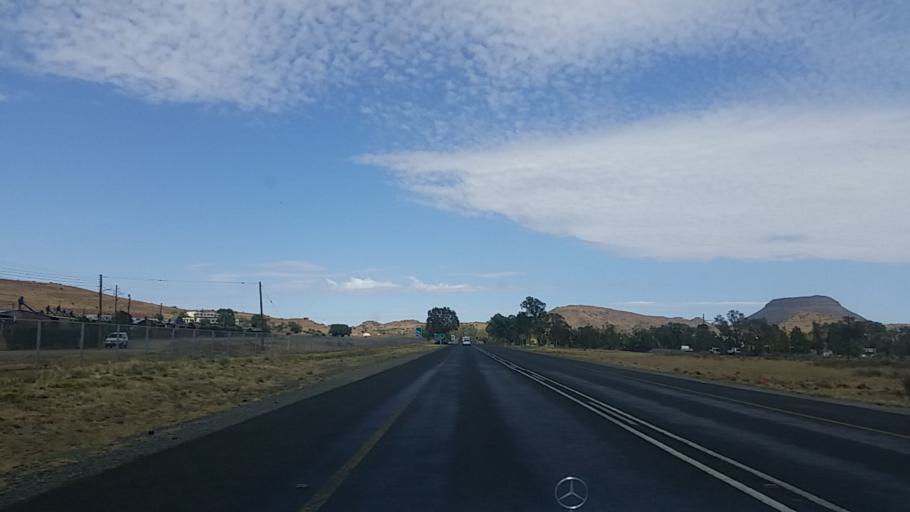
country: ZA
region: Northern Cape
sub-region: Pixley ka Seme District Municipality
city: Colesberg
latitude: -30.7066
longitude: 25.1121
